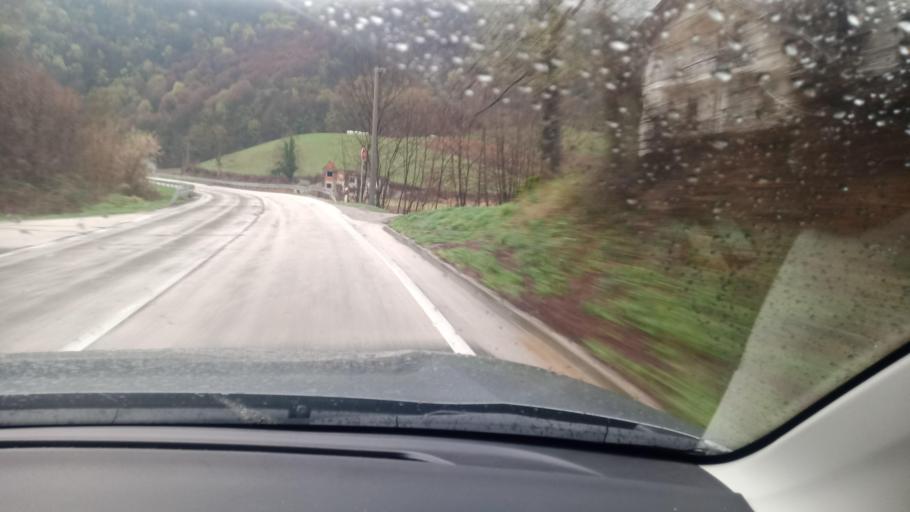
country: BA
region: Federation of Bosnia and Herzegovina
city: Bosanska Krupa
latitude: 44.9248
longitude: 16.1487
